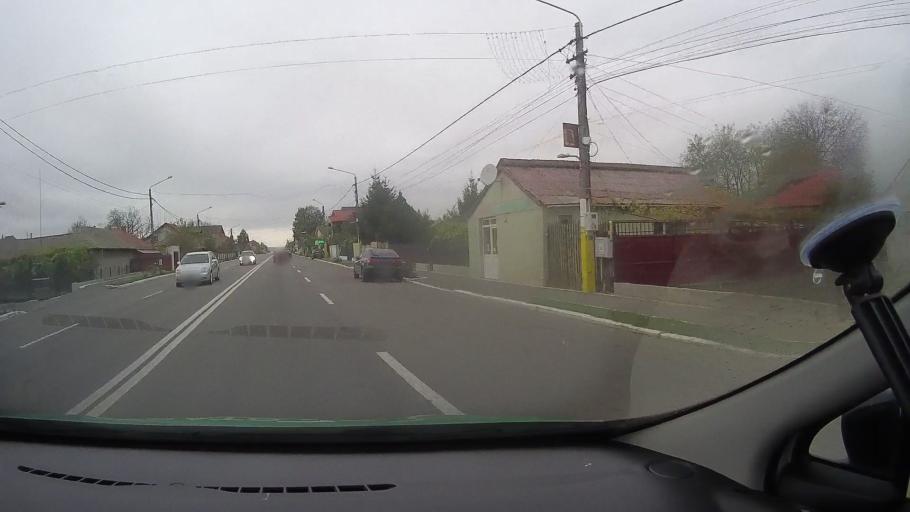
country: RO
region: Constanta
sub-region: Comuna Valu lui Traian
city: Valu lui Traian
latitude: 44.1671
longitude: 28.4560
